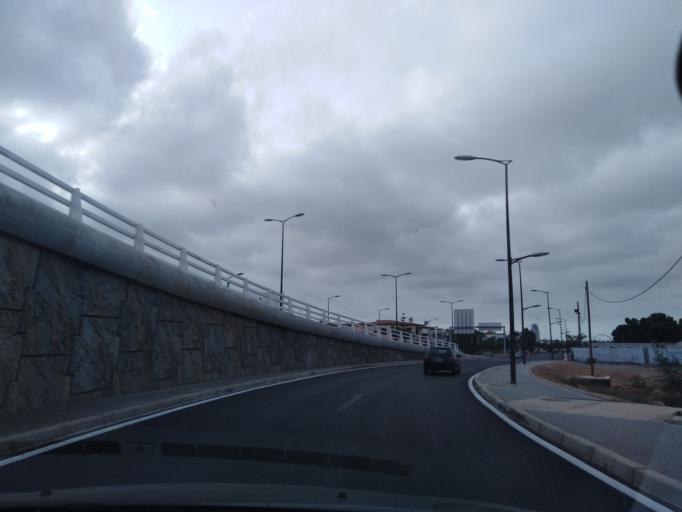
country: MA
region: Grand Casablanca
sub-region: Casablanca
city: Casablanca
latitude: 33.5396
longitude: -7.6631
